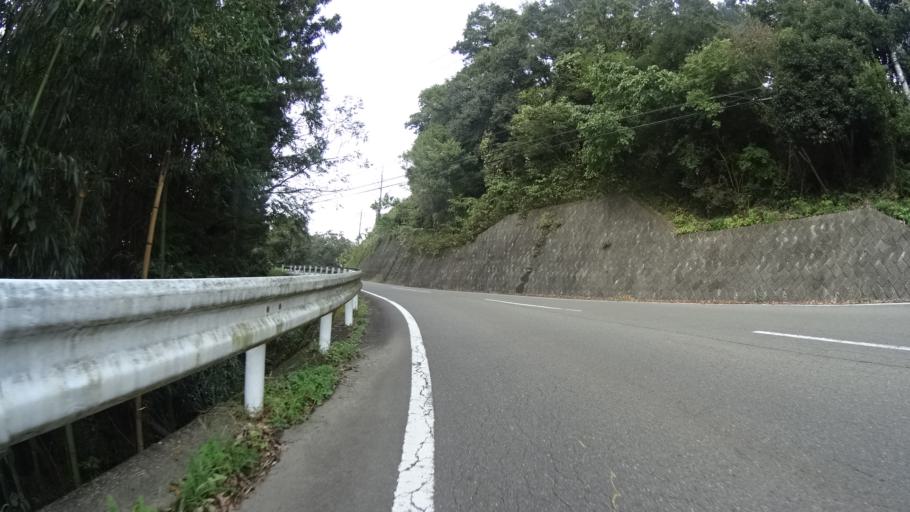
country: JP
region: Yamanashi
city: Uenohara
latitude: 35.6317
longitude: 139.0601
